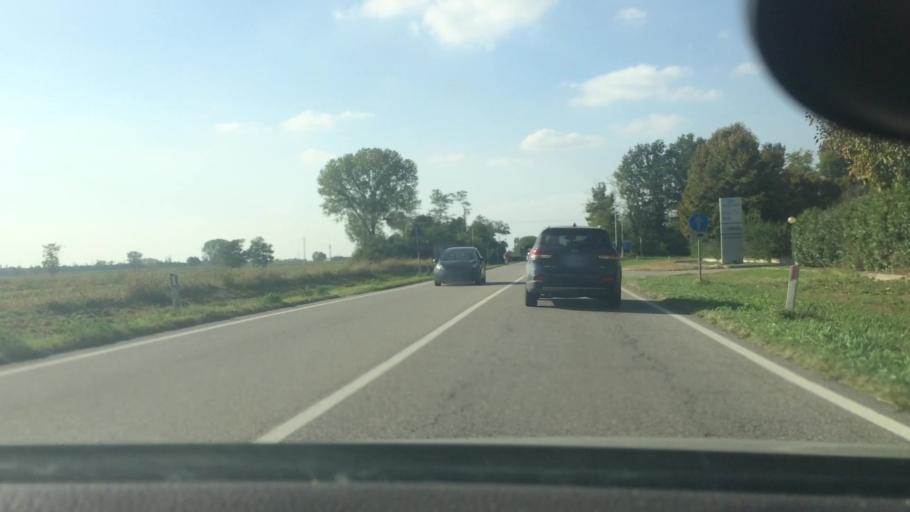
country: IT
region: Lombardy
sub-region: Citta metropolitana di Milano
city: Arconate
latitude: 45.5308
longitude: 8.8341
